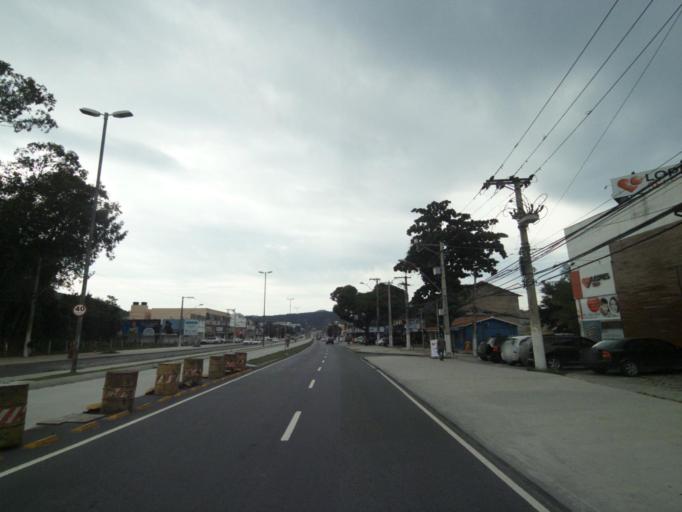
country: BR
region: Rio de Janeiro
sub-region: Niteroi
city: Niteroi
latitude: -22.9352
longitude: -43.0643
